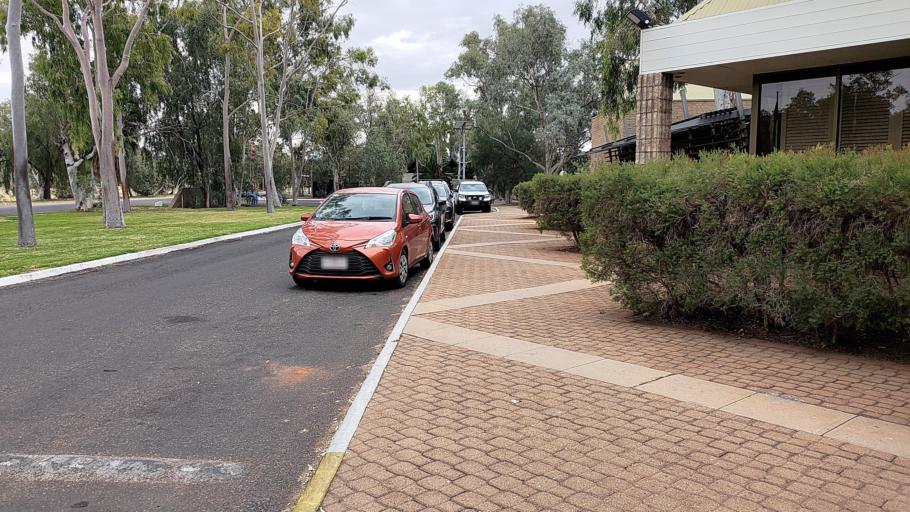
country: AU
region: Northern Territory
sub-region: Alice Springs
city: Alice Springs
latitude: -23.7151
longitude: 133.8792
